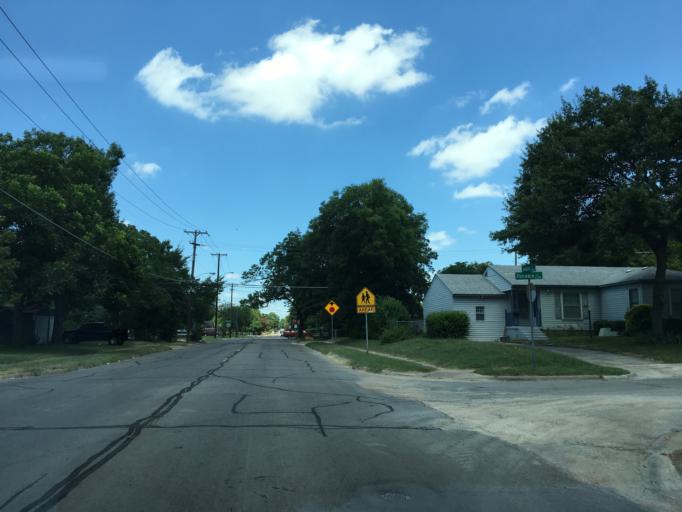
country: US
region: Texas
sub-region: Dallas County
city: Garland
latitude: 32.8418
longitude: -96.6731
